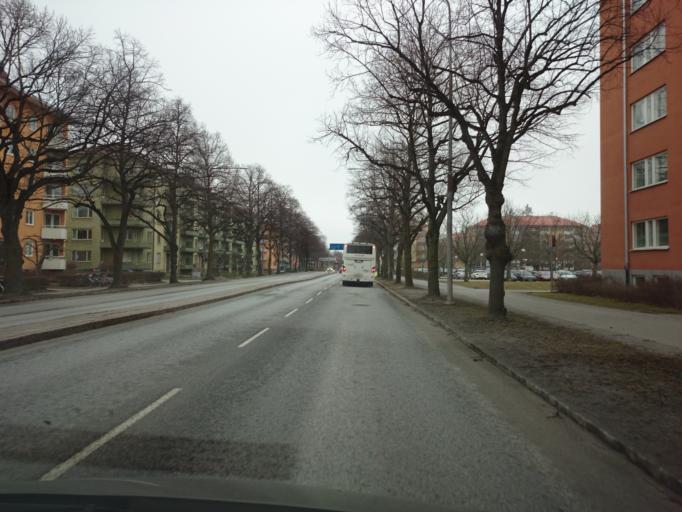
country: SE
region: Uppsala
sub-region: Uppsala Kommun
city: Uppsala
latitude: 59.8597
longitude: 17.6171
